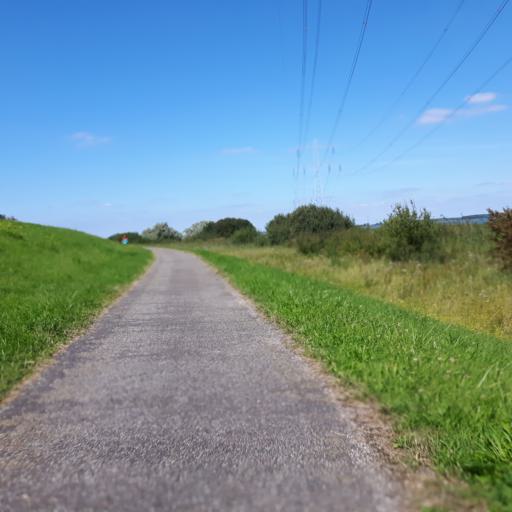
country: NL
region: North Brabant
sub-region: Gemeente Bergen op Zoom
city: Bergen op Zoom
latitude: 51.4550
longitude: 4.2376
